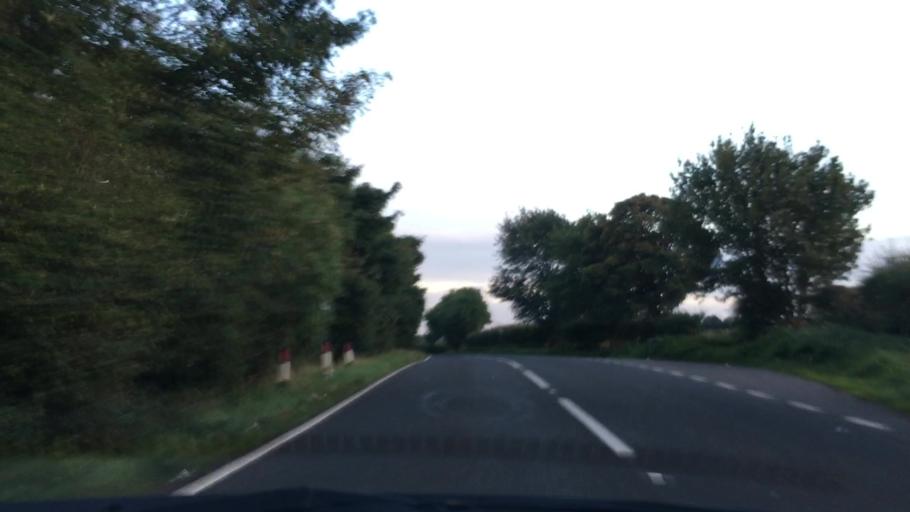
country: GB
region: England
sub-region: North East Lincolnshire
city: Wold Newton
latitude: 53.4774
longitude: -0.1186
